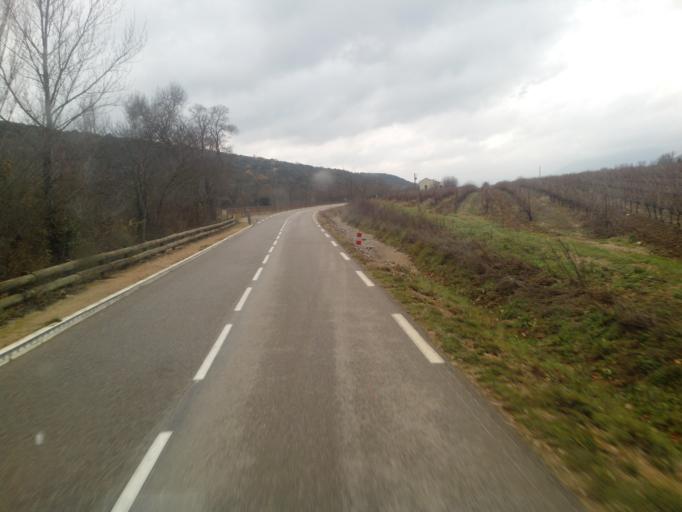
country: FR
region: Languedoc-Roussillon
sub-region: Departement de l'Herault
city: Saint-Bauzille-de-Putois
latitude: 43.9229
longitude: 3.7910
